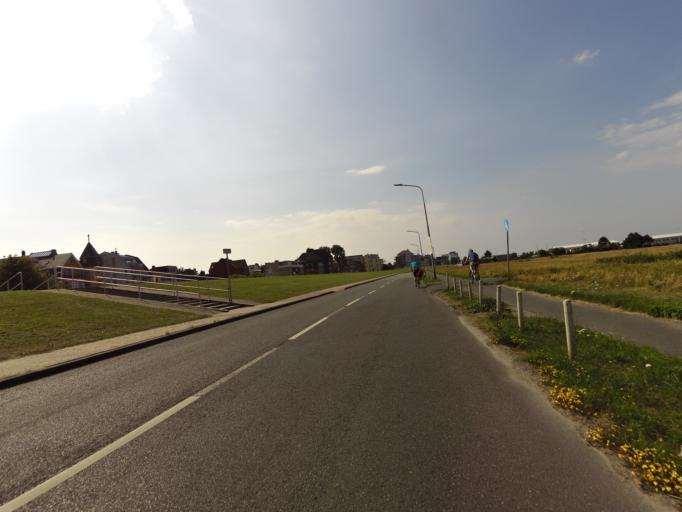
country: DE
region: Lower Saxony
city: Cuxhaven
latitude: 53.8715
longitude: 8.7046
